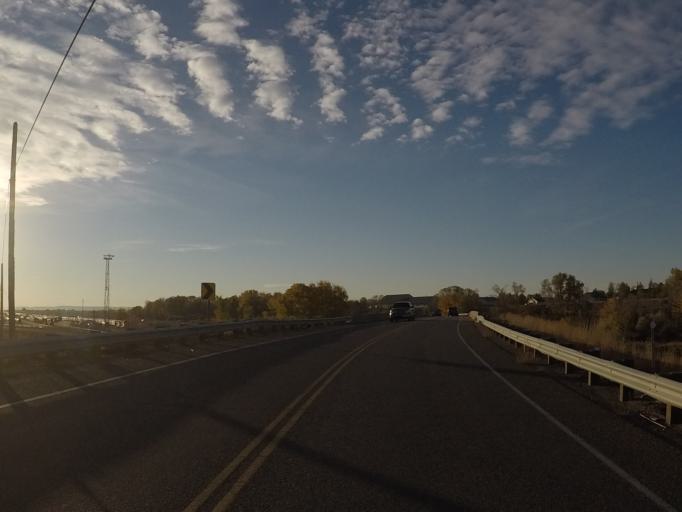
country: US
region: Montana
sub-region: Yellowstone County
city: Laurel
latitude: 45.6822
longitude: -108.7129
